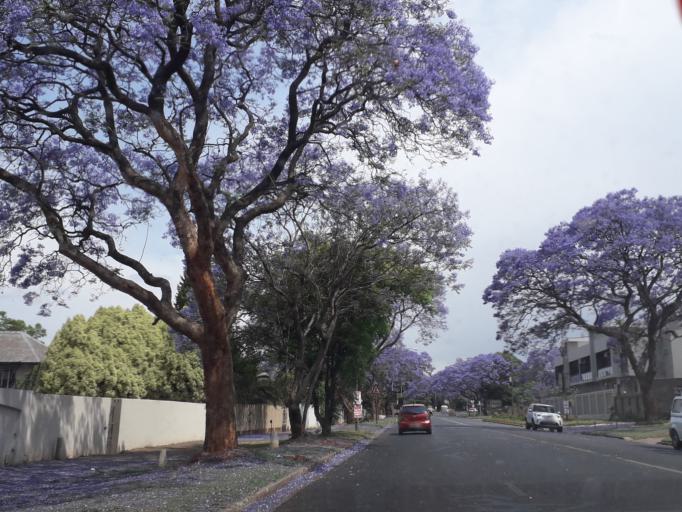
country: ZA
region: Gauteng
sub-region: City of Johannesburg Metropolitan Municipality
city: Johannesburg
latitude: -26.1646
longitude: 28.0137
